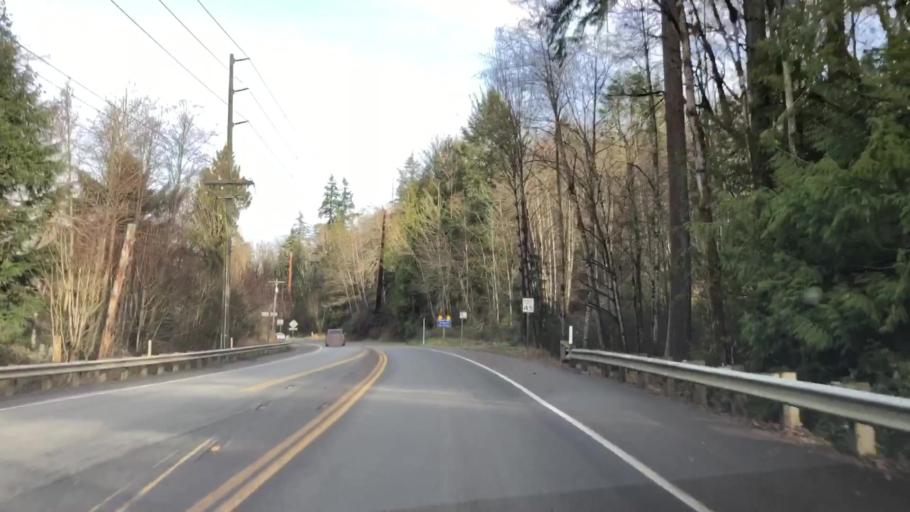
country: US
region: Washington
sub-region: Kitsap County
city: Indianola
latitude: 47.7750
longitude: -122.5561
